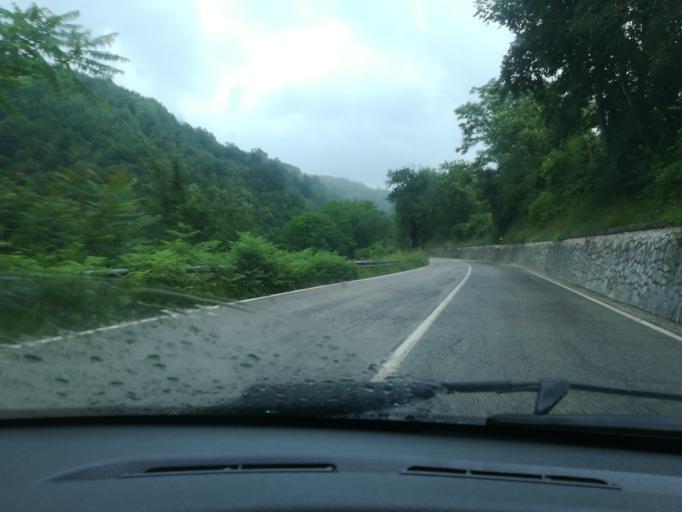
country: IT
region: The Marches
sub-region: Province of Fermo
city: Amandola
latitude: 42.9825
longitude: 13.3477
